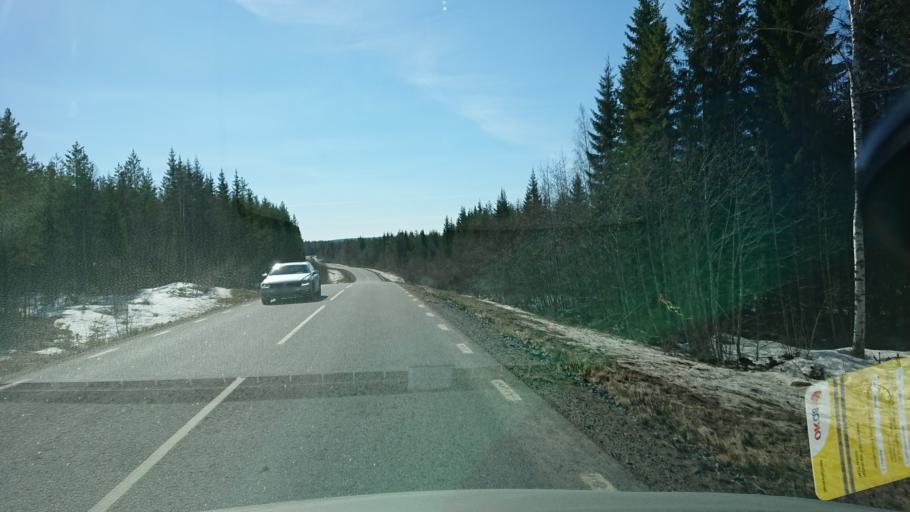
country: SE
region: Vaesternorrland
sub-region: Solleftea Kommun
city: As
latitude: 63.6841
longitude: 16.4324
